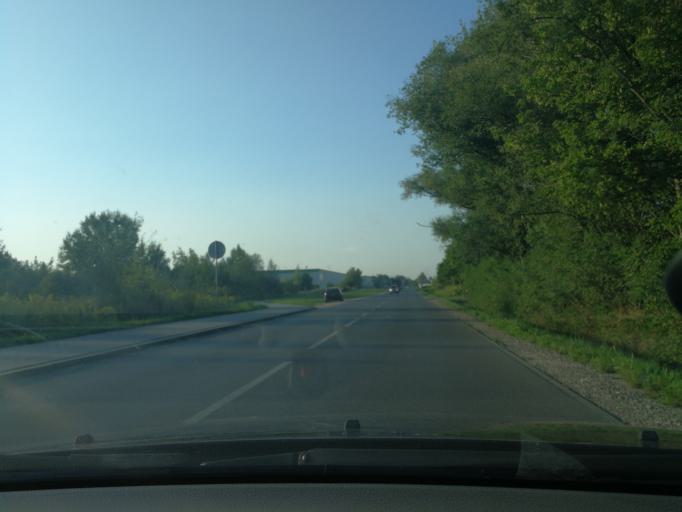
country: PL
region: Masovian Voivodeship
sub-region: Powiat pruszkowski
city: Brwinow
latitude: 52.1729
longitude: 20.7503
